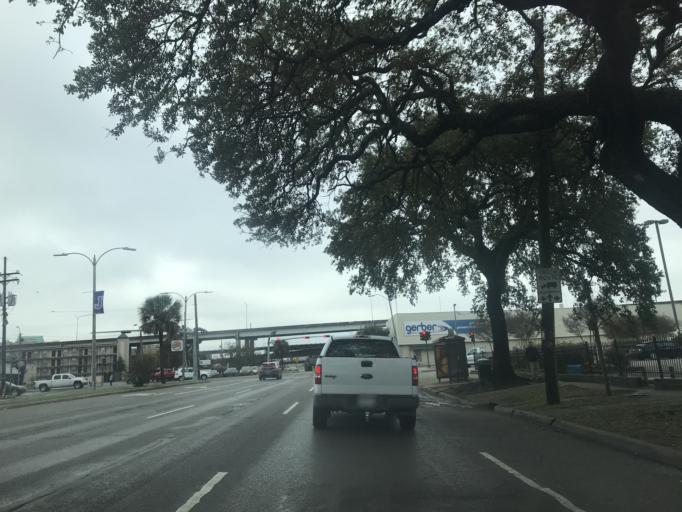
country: US
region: Louisiana
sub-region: Orleans Parish
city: New Orleans
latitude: 29.9696
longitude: -90.1061
